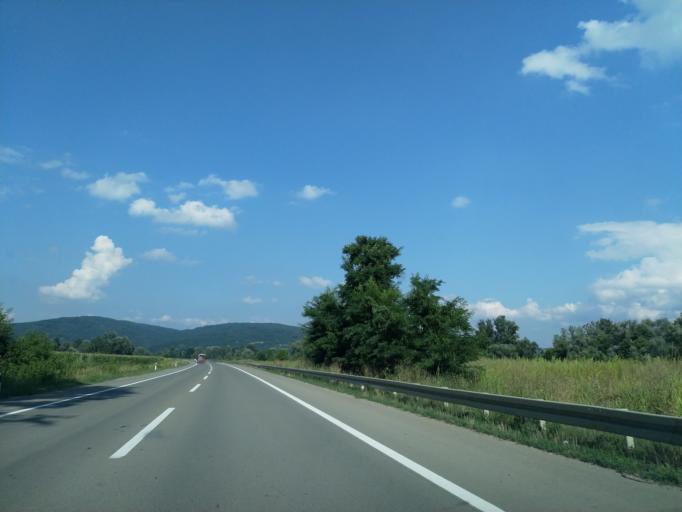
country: RS
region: Central Serbia
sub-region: Rasinski Okrug
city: Krusevac
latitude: 43.6110
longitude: 21.3458
